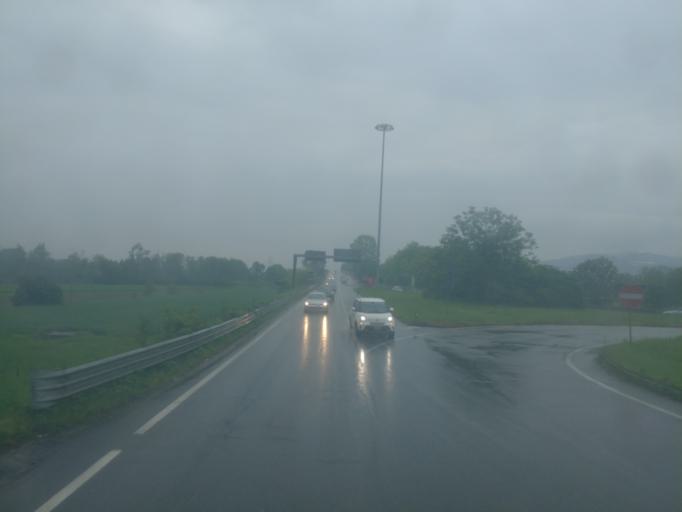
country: IT
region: Piedmont
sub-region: Provincia di Torino
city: Tagliaferro
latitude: 44.9674
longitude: 7.6694
